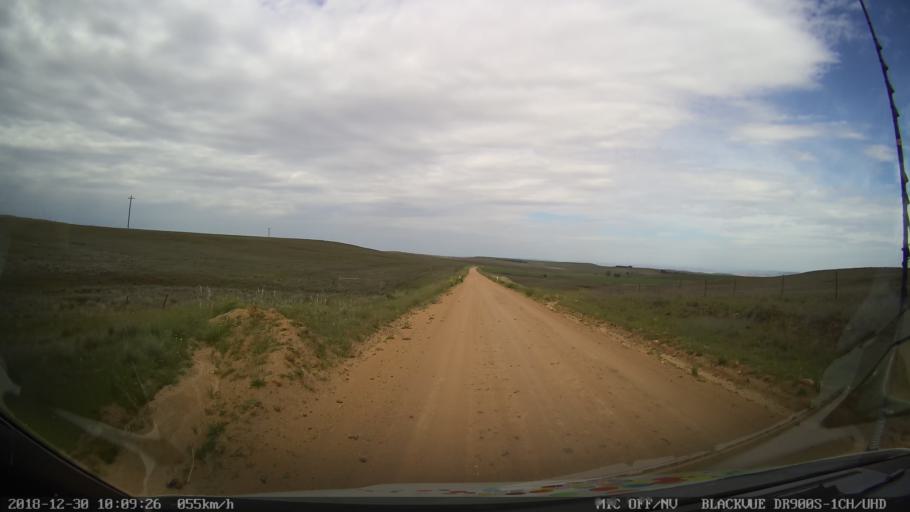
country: AU
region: New South Wales
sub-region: Cooma-Monaro
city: Cooma
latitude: -36.5483
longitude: 149.1054
